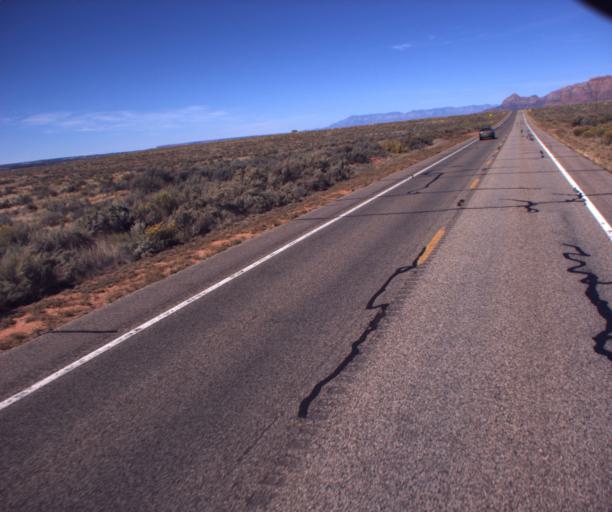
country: US
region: Arizona
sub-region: Mohave County
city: Colorado City
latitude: 36.9097
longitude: -112.9267
